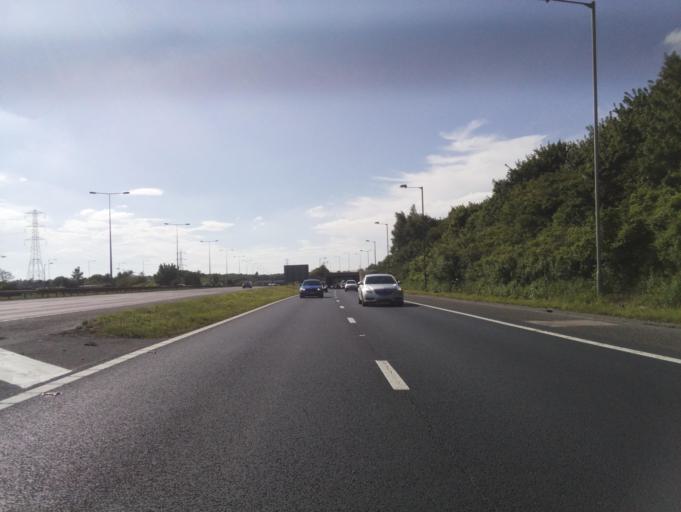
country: GB
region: England
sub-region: Borough of Bolton
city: Kearsley
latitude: 53.5312
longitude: -2.3770
